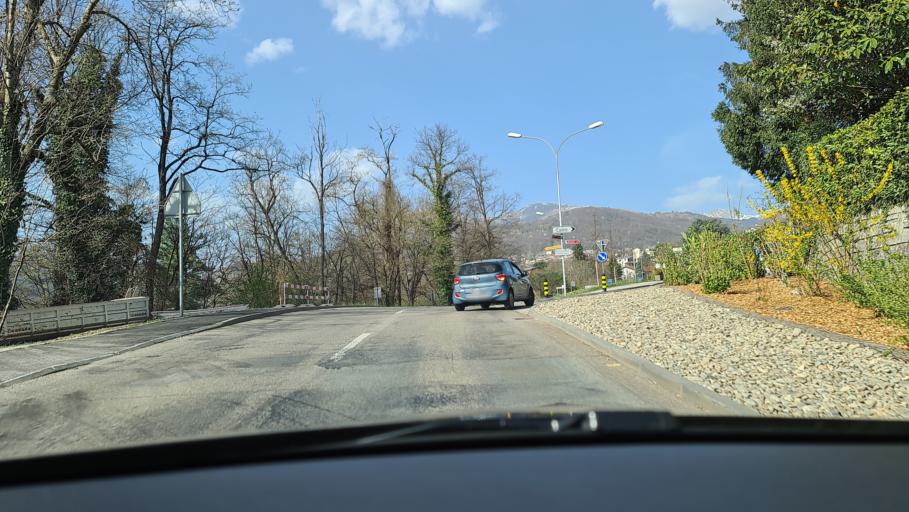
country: CH
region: Ticino
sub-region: Lugano District
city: Cadro
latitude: 46.0401
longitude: 8.9821
